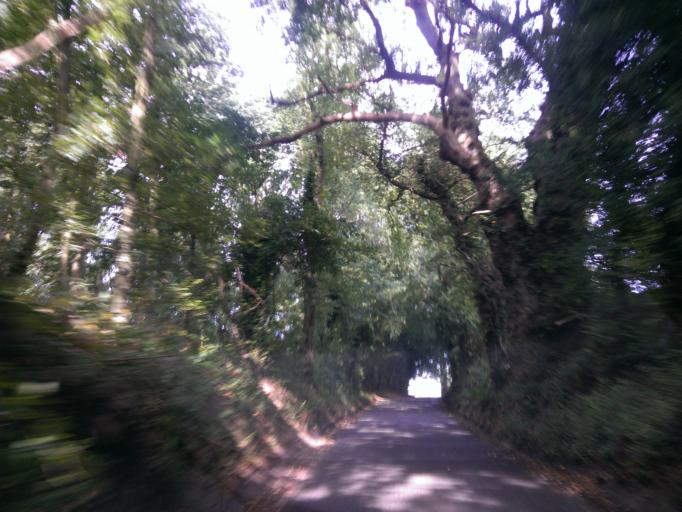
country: GB
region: England
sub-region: Essex
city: Sible Hedingham
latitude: 51.9664
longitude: 0.6243
